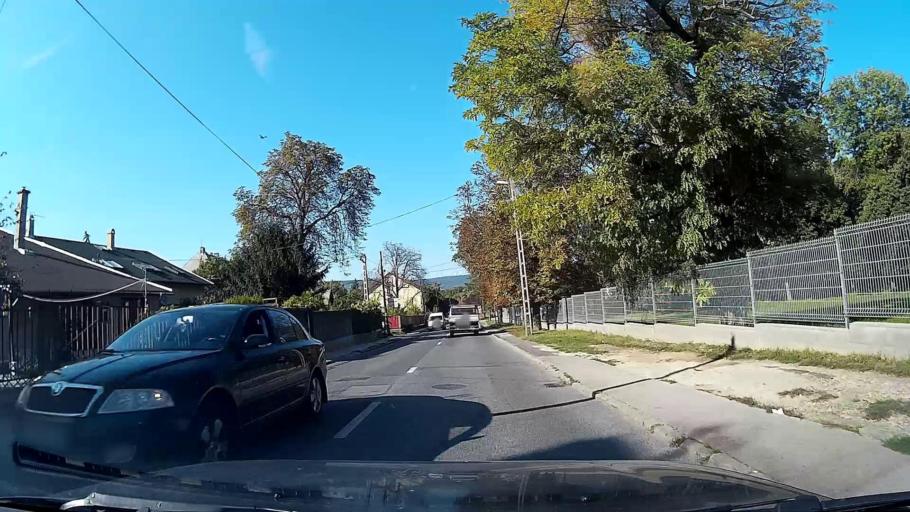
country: HU
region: Pest
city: Budaors
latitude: 47.4387
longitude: 18.9792
